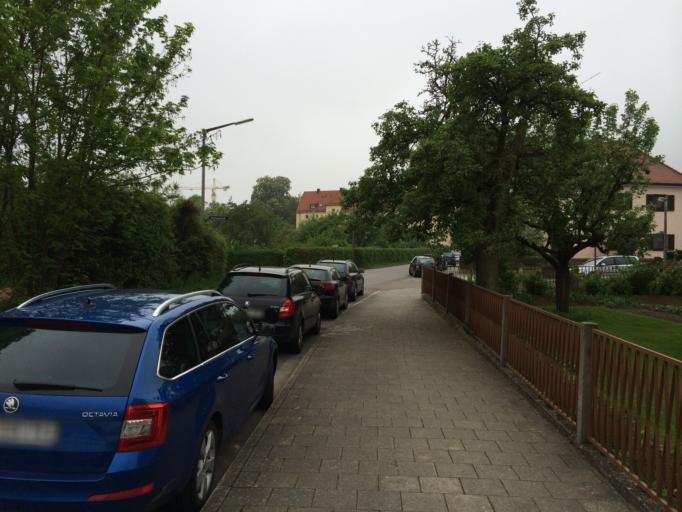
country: DE
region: Bavaria
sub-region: Upper Palatinate
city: Pentling
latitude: 49.0030
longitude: 12.0877
